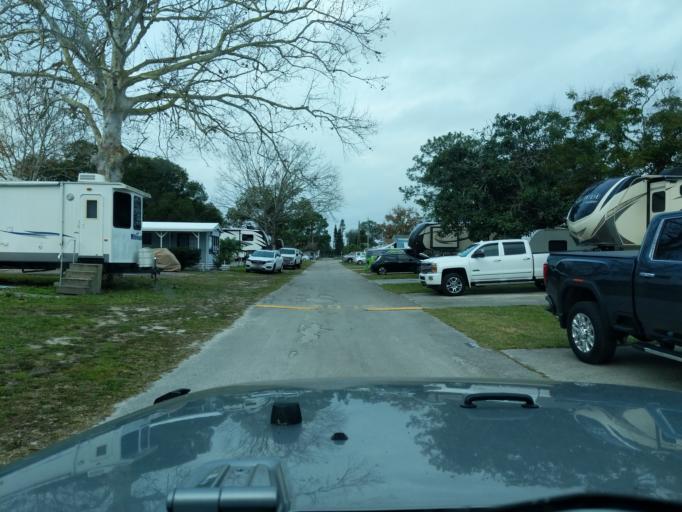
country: US
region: Florida
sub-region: Orange County
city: Winter Garden
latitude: 28.5546
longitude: -81.5884
